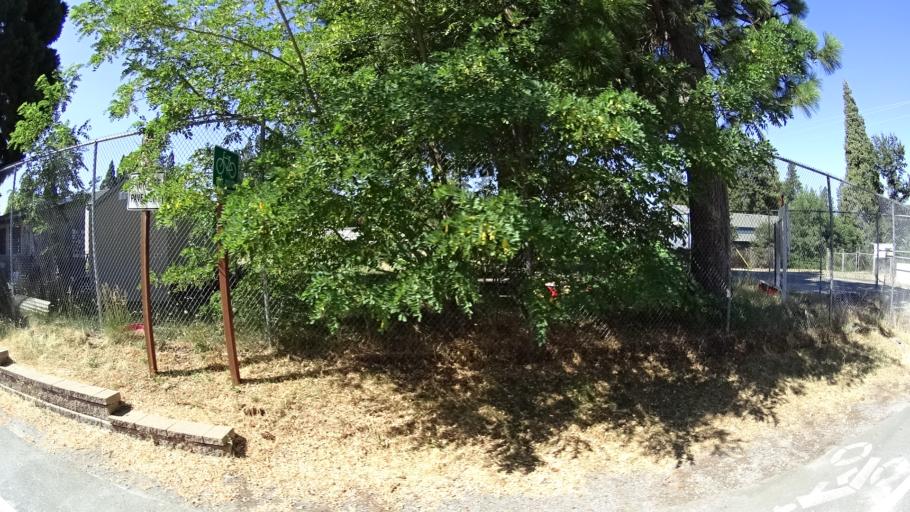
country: US
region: California
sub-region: Amador County
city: Pioneer
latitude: 38.3991
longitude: -120.5267
